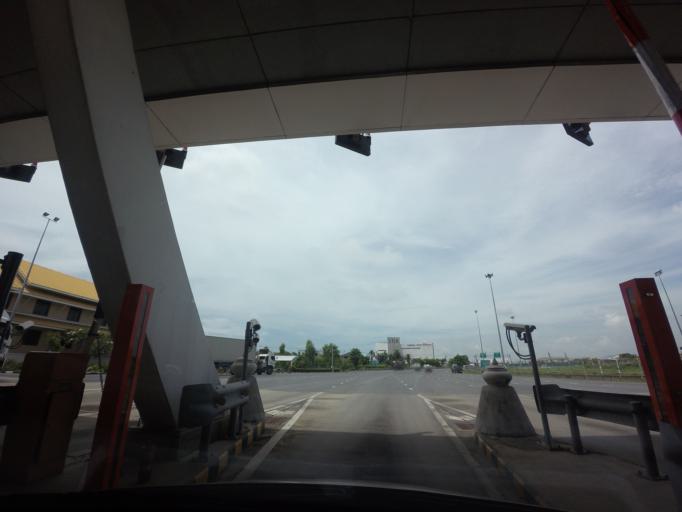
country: TH
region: Bangkok
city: Thung Khru
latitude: 13.6263
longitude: 100.5250
